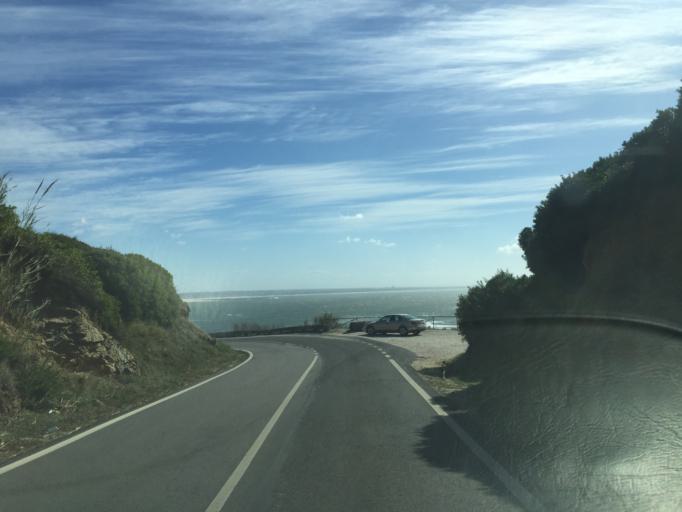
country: PT
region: Coimbra
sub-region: Figueira da Foz
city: Buarcos
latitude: 40.1796
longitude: -8.9044
